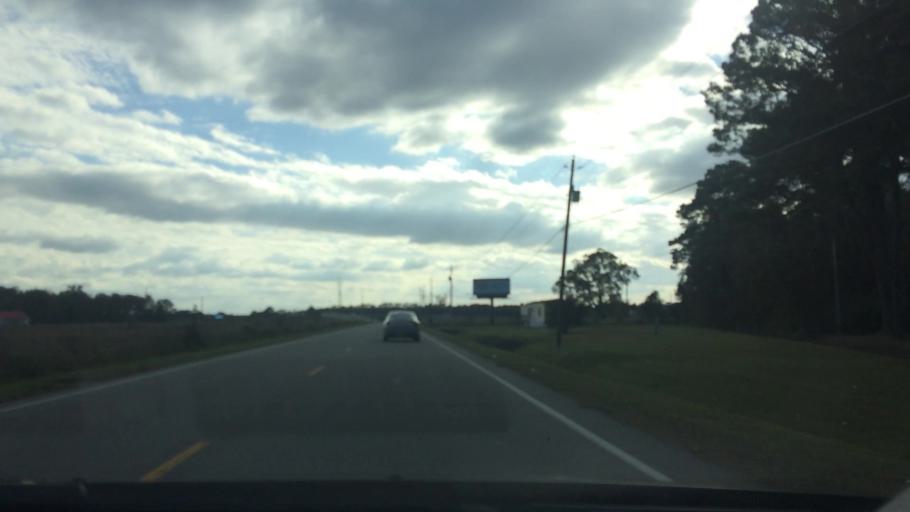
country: US
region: North Carolina
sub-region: Wayne County
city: Elroy
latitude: 35.4192
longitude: -77.8933
